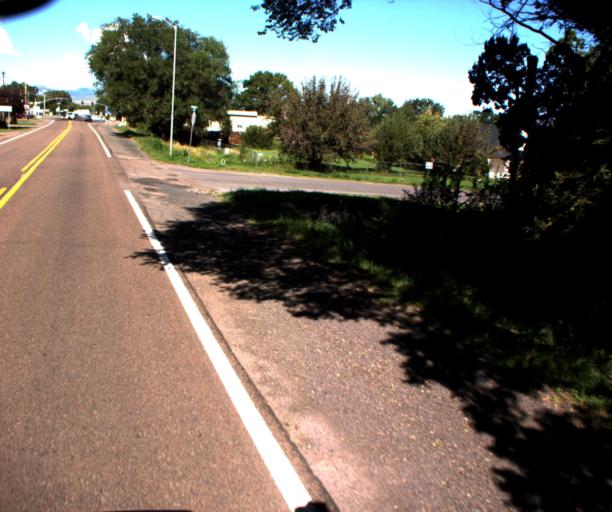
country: US
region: Arizona
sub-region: Apache County
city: Eagar
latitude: 34.1110
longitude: -109.2892
